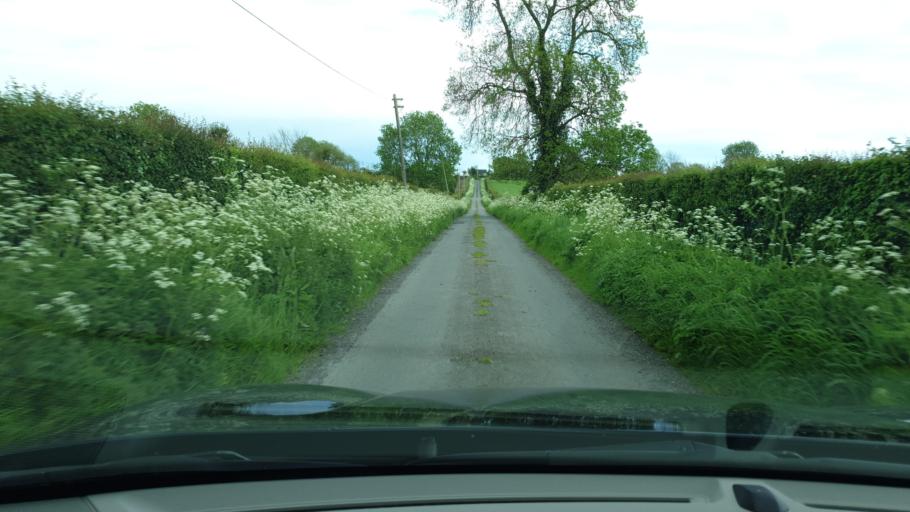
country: IE
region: Leinster
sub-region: An Mhi
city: Ratoath
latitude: 53.5268
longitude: -6.4611
